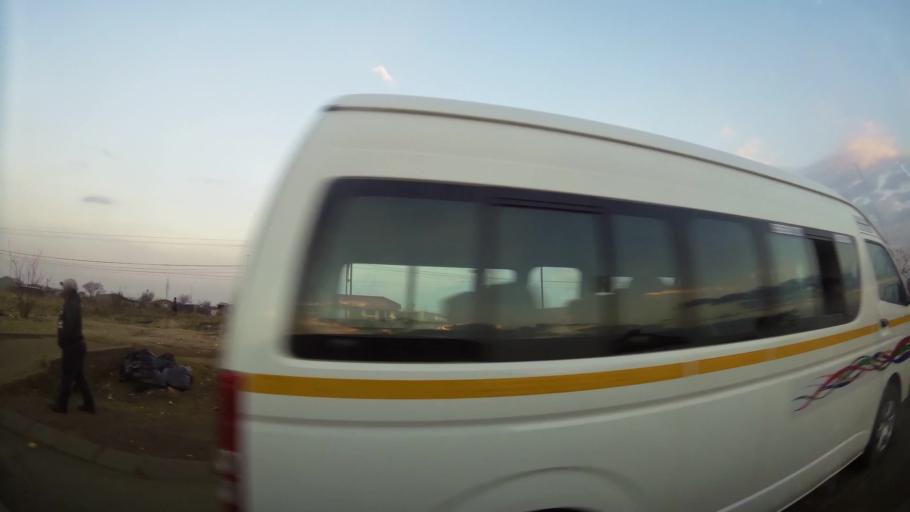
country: ZA
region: Gauteng
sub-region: City of Johannesburg Metropolitan Municipality
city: Orange Farm
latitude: -26.5563
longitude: 27.8789
